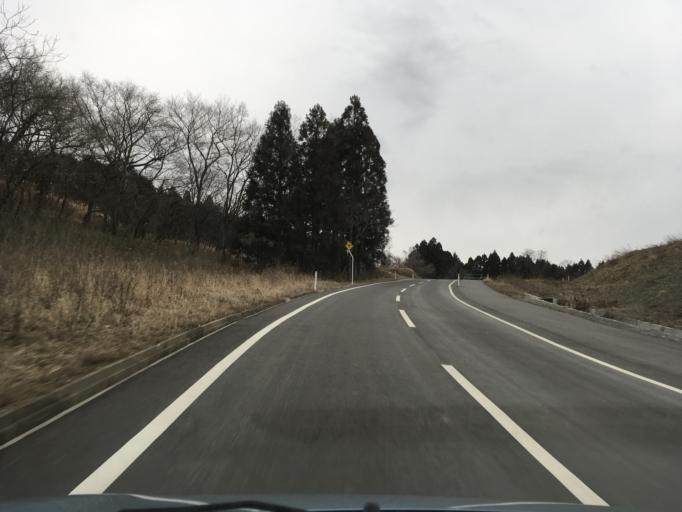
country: JP
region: Miyagi
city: Wakuya
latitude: 38.6693
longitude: 141.2772
